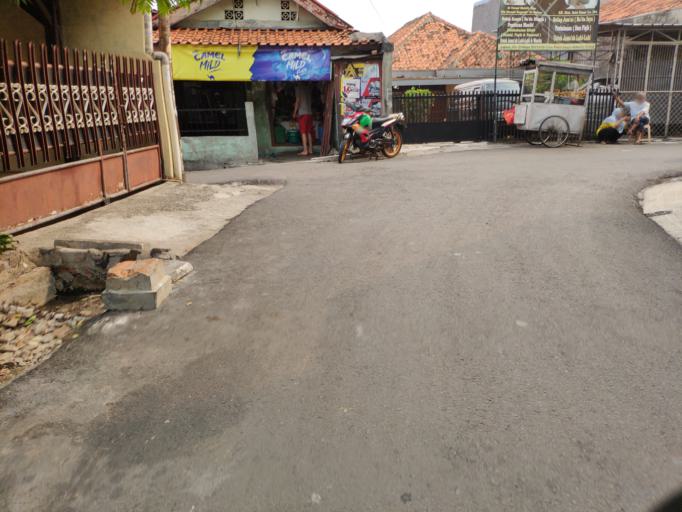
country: ID
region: Jakarta Raya
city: Jakarta
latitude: -6.1953
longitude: 106.8673
